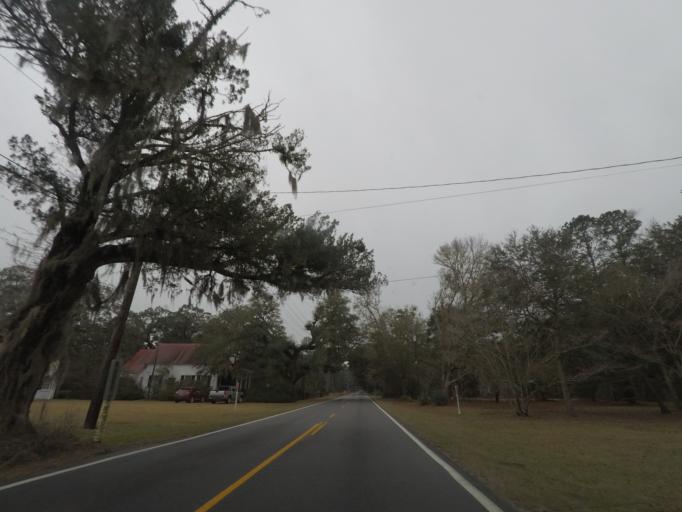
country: US
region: South Carolina
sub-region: Charleston County
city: Hollywood
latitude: 32.7173
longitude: -80.3491
